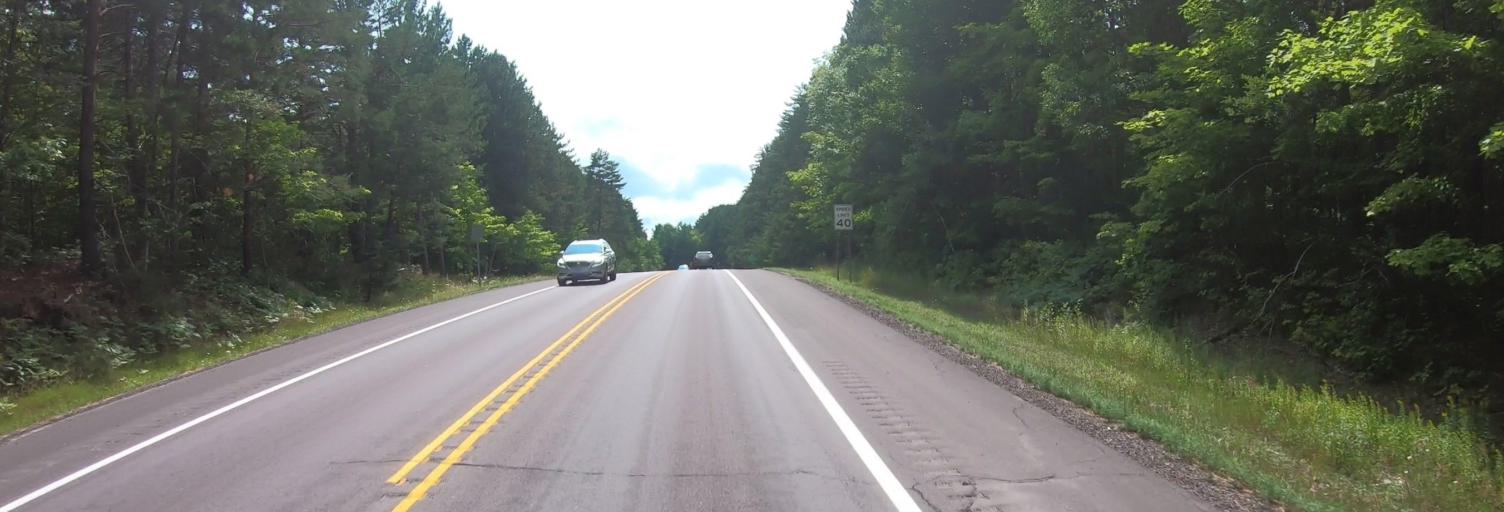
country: US
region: Michigan
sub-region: Houghton County
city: Hancock
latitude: 47.0493
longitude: -88.6702
